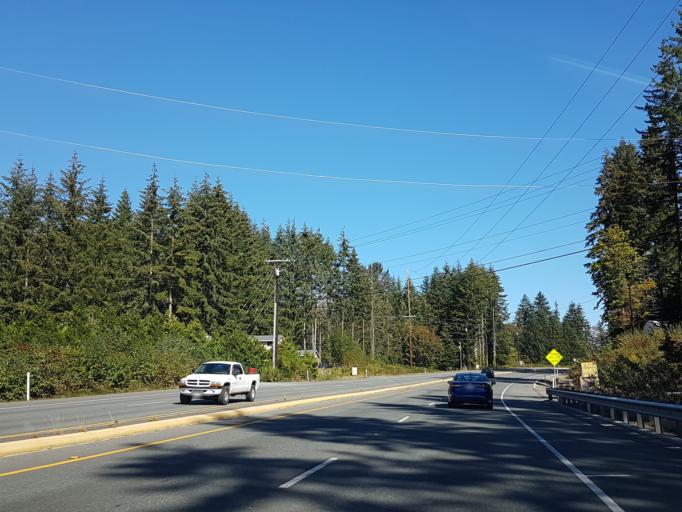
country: US
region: Washington
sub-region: Snohomish County
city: Clearview
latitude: 47.8229
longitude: -122.1361
